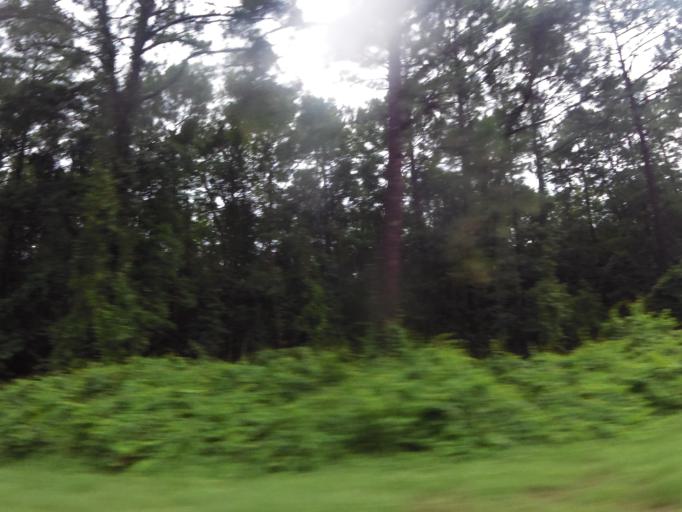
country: US
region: Florida
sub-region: Duval County
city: Jacksonville Beach
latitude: 30.2627
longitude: -81.5036
